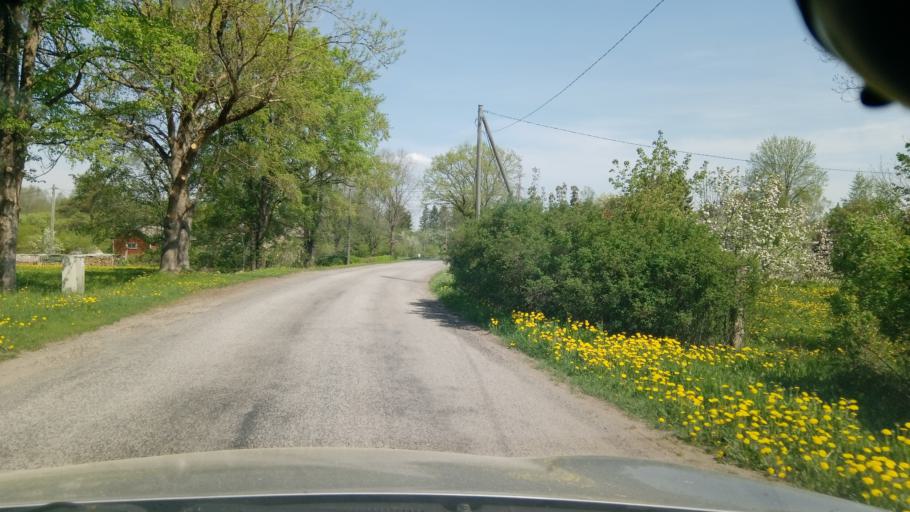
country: EE
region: Laeaene-Virumaa
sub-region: Tapa vald
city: Tapa
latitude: 59.1929
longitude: 25.8392
